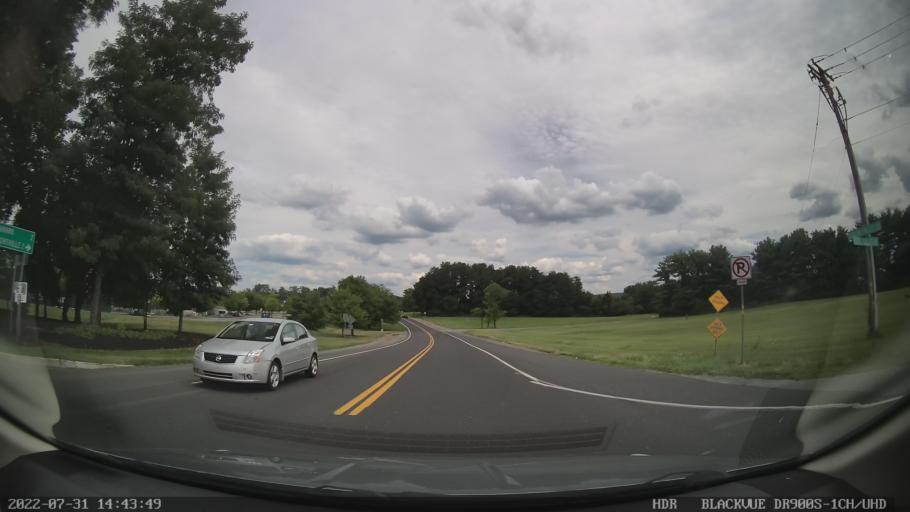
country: US
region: Pennsylvania
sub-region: Lehigh County
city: Fountain Hill
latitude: 40.5576
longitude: -75.4053
